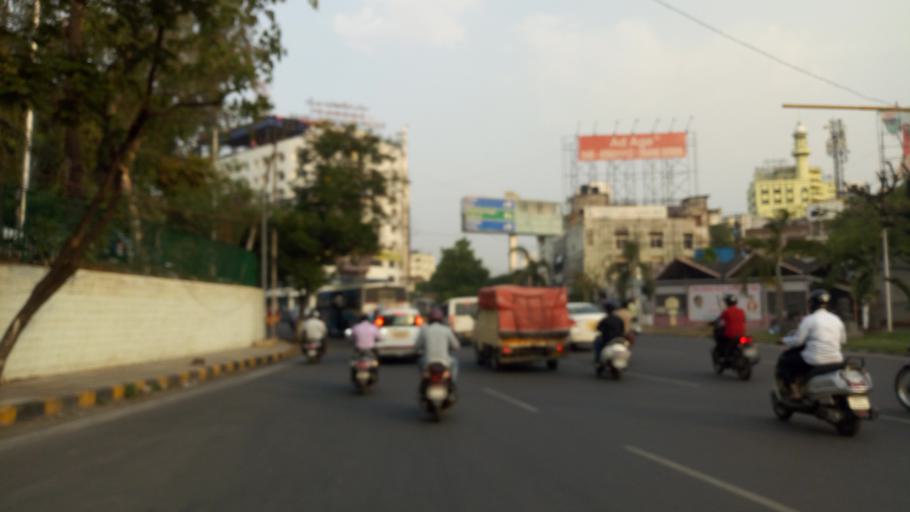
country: IN
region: Telangana
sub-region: Hyderabad
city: Hyderabad
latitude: 17.3992
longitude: 78.4712
